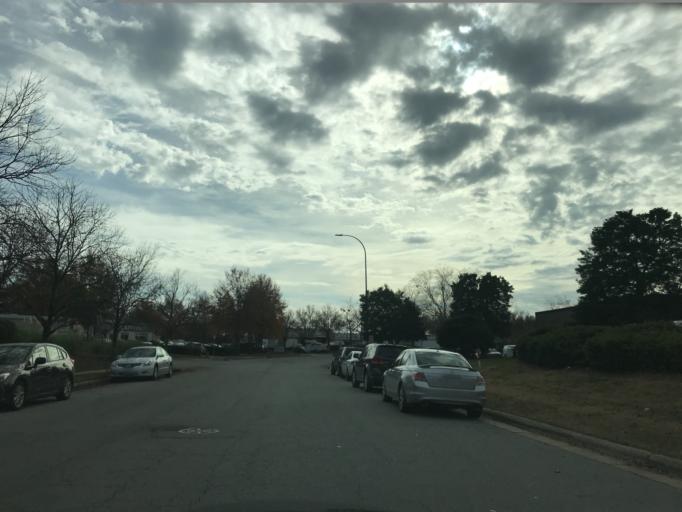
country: US
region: North Carolina
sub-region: Wake County
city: Raleigh
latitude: 35.8527
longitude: -78.5845
